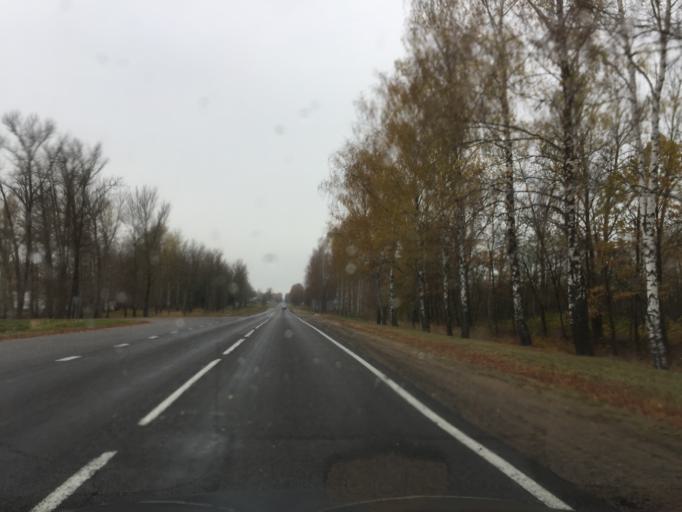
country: BY
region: Mogilev
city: Slawharad
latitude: 53.3460
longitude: 30.8129
